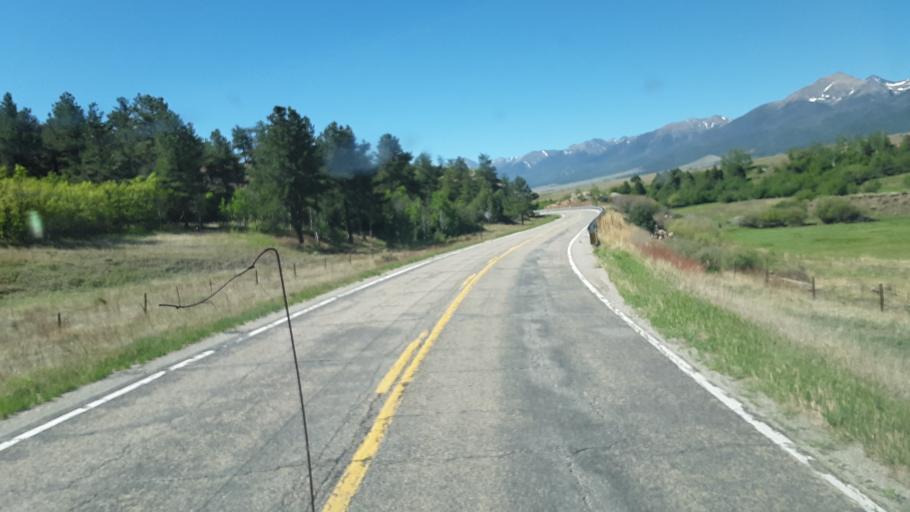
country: US
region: Colorado
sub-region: Custer County
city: Westcliffe
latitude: 38.2302
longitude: -105.5544
